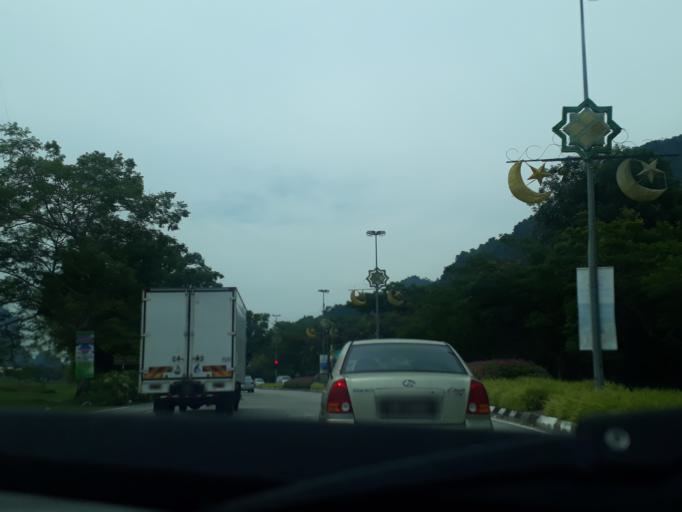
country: MY
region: Perak
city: Ipoh
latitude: 4.6252
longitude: 101.1524
